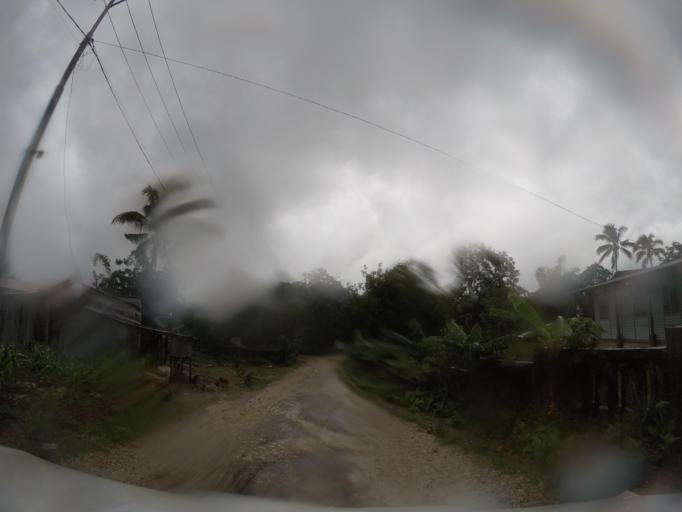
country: TL
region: Baucau
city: Venilale
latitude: -8.6403
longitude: 126.3901
